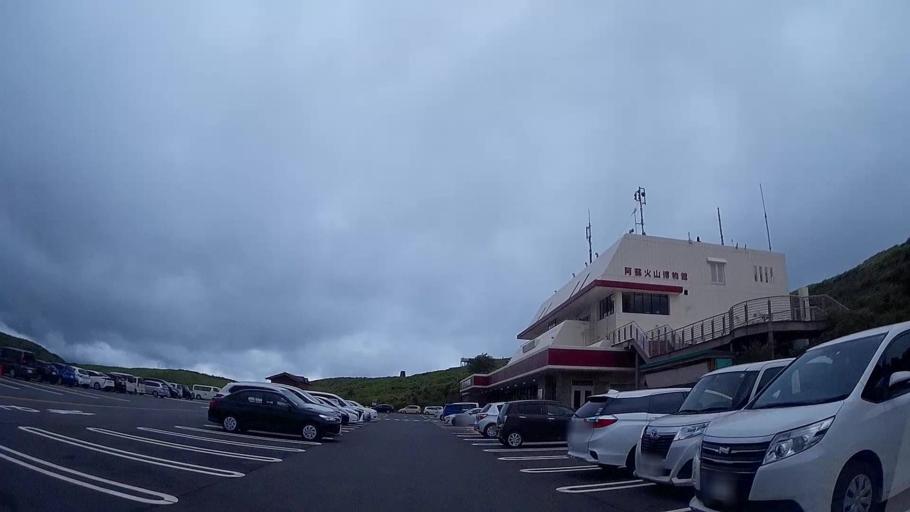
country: JP
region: Kumamoto
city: Aso
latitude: 32.8855
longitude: 131.0528
